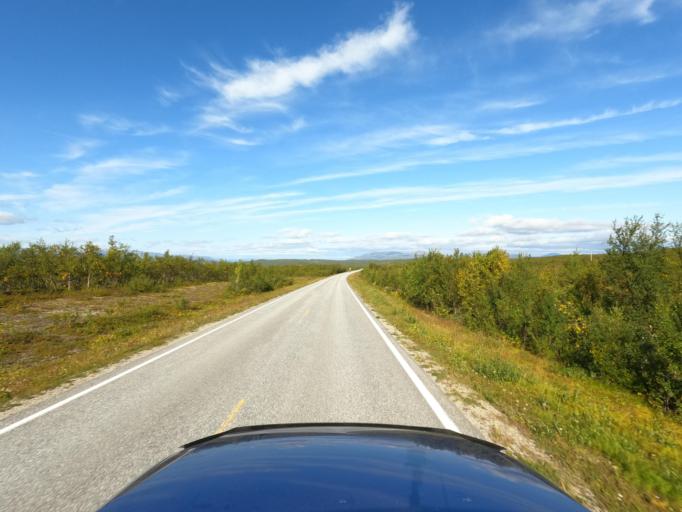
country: NO
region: Finnmark Fylke
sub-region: Karasjok
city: Karasjohka
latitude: 69.7260
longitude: 25.2352
